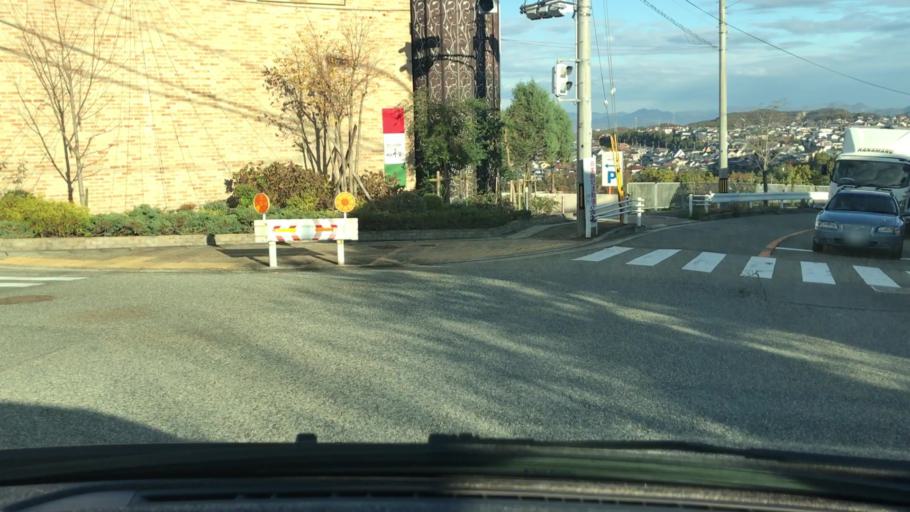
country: JP
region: Hyogo
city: Sandacho
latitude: 34.8229
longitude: 135.2504
